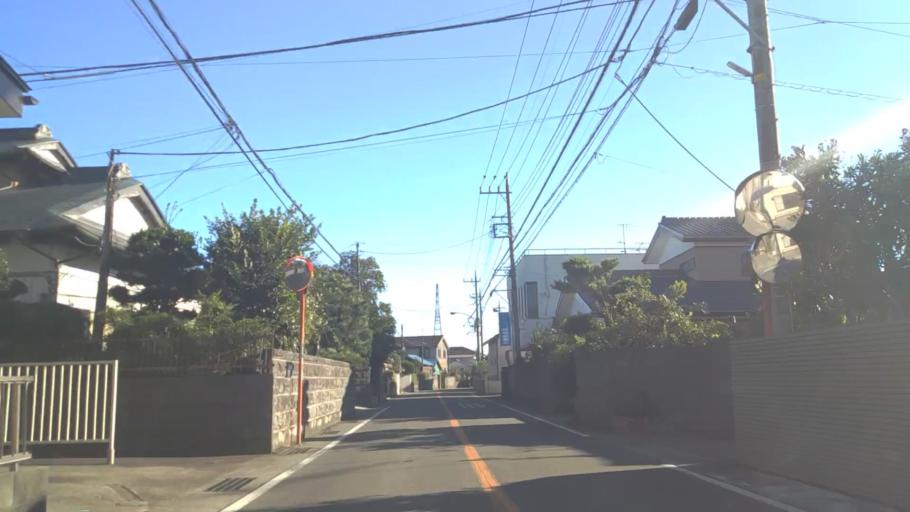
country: JP
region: Kanagawa
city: Atsugi
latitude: 35.4155
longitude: 139.3655
